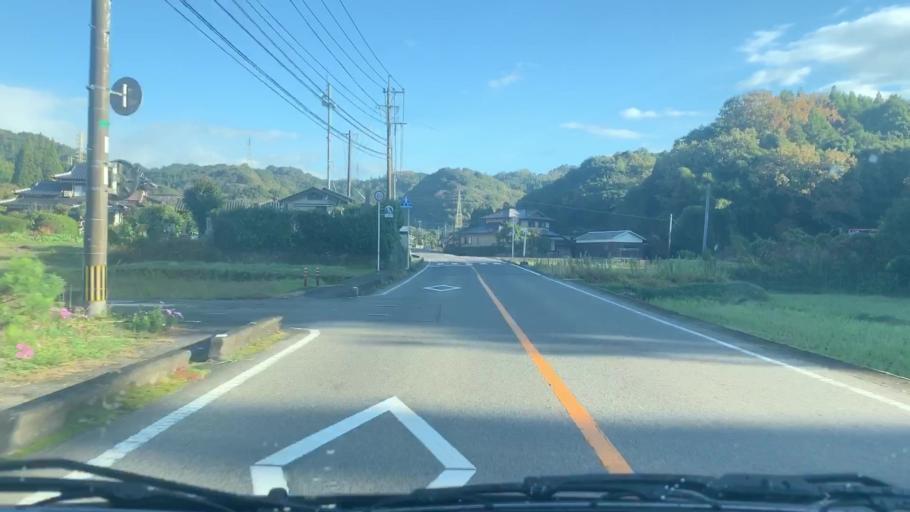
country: JP
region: Saga Prefecture
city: Takeocho-takeo
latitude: 33.2316
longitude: 130.0607
